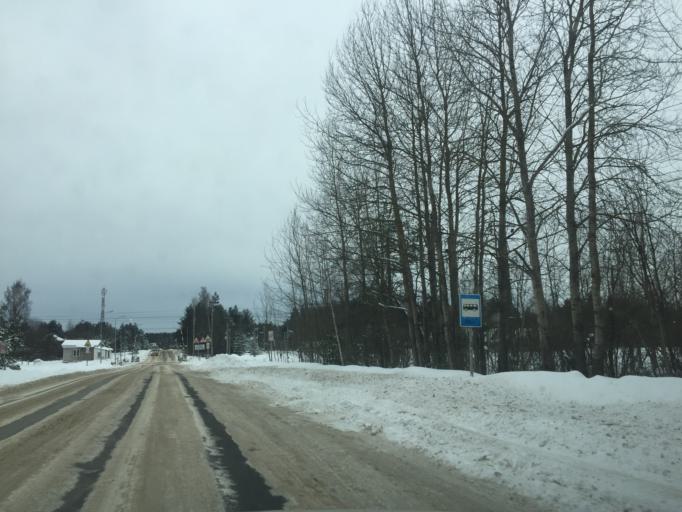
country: RU
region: Leningrad
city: Imeni Sverdlova
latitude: 59.8653
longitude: 30.6710
